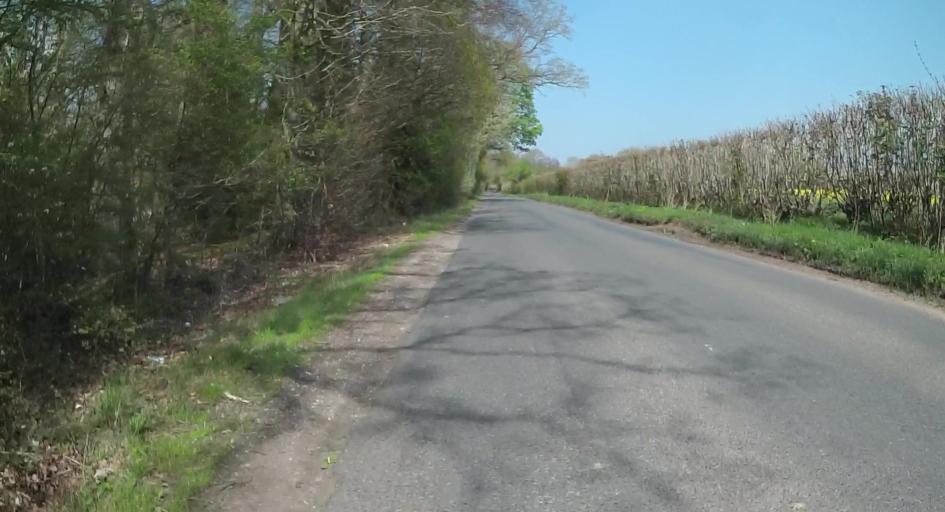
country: GB
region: England
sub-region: Hampshire
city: Basingstoke
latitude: 51.3180
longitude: -1.0802
